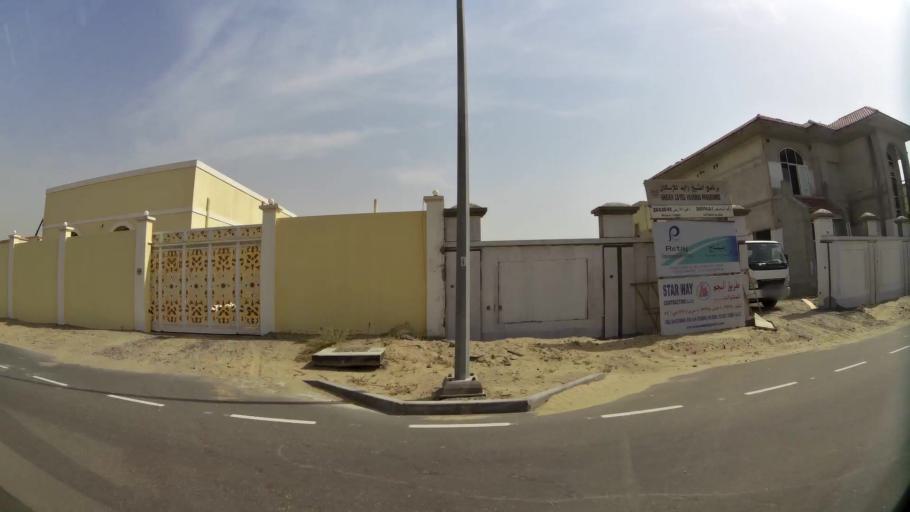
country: AE
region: Ash Shariqah
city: Sharjah
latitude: 25.2691
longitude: 55.4667
